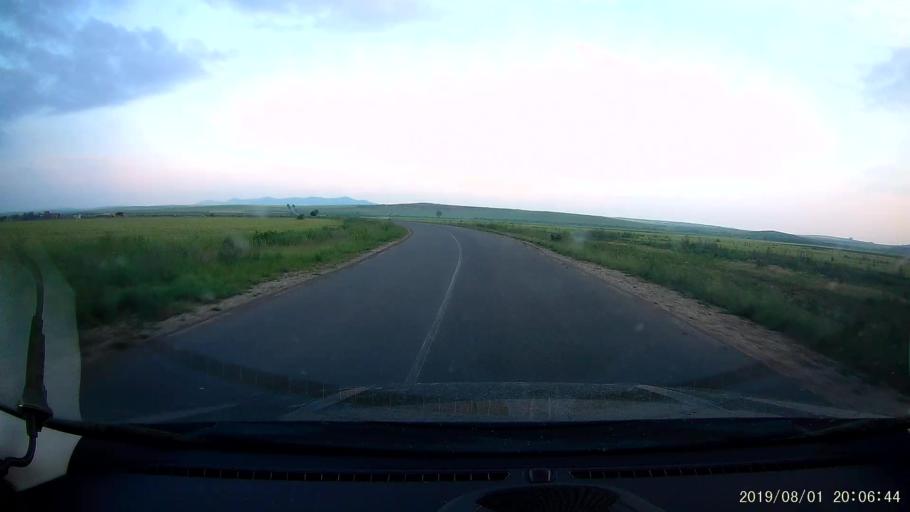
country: BG
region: Yambol
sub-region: Obshtina Yambol
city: Yambol
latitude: 42.5315
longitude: 26.5576
